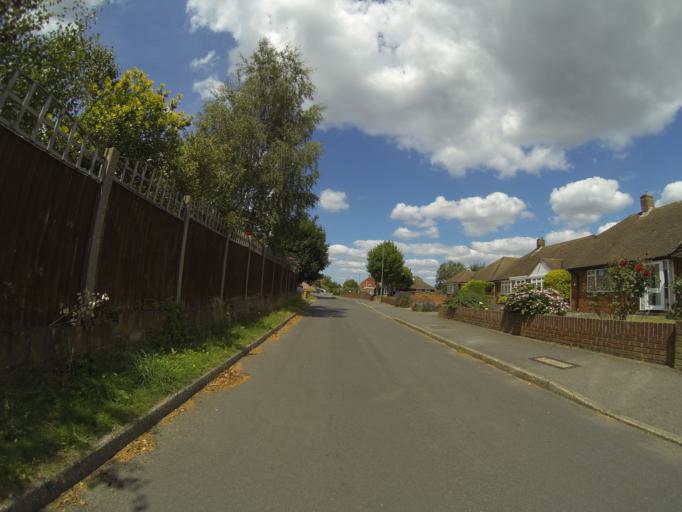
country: GB
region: England
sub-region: Kent
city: Swanley
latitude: 51.4246
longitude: 0.1732
